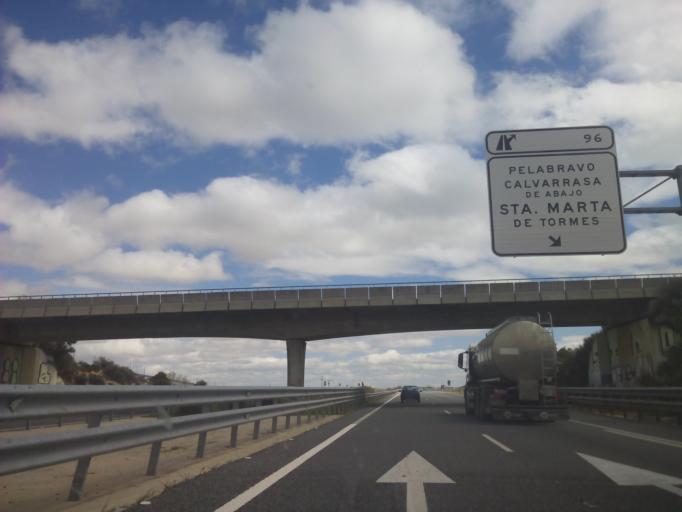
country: ES
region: Castille and Leon
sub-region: Provincia de Salamanca
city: Santa Marta de Tormes
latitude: 40.9444
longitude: -5.6082
